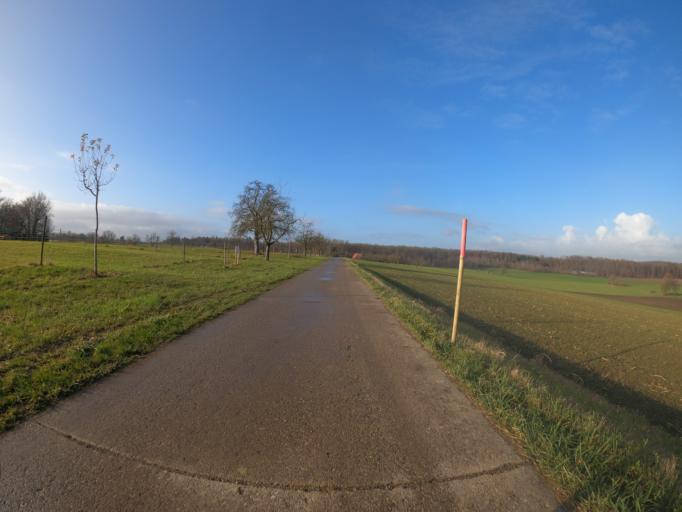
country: DE
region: Baden-Wuerttemberg
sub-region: Regierungsbezirk Stuttgart
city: Hattenhofen
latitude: 48.6703
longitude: 9.5553
